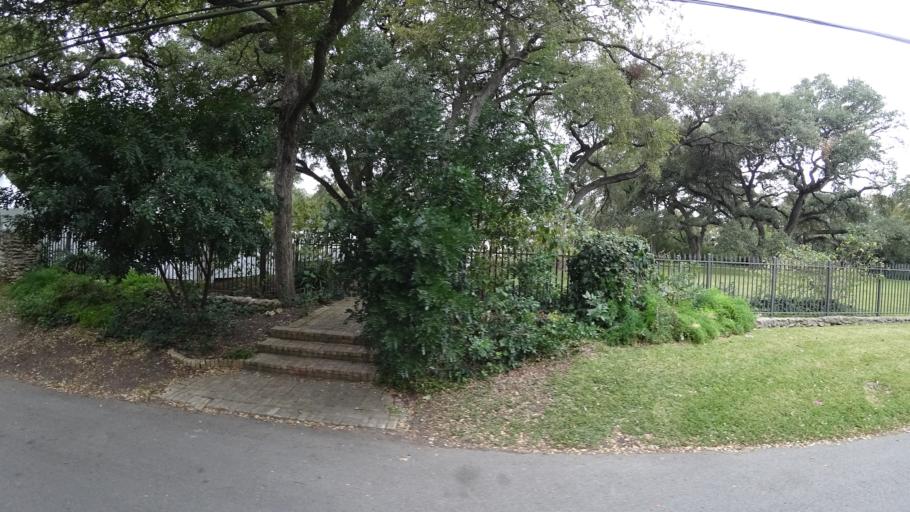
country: US
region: Texas
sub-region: Travis County
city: Austin
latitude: 30.2869
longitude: -97.7575
